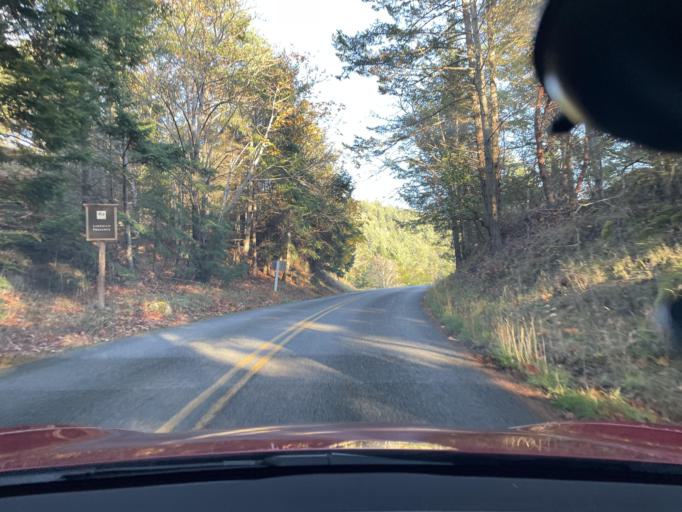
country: US
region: Washington
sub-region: San Juan County
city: Friday Harbor
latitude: 48.5146
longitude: -123.1477
